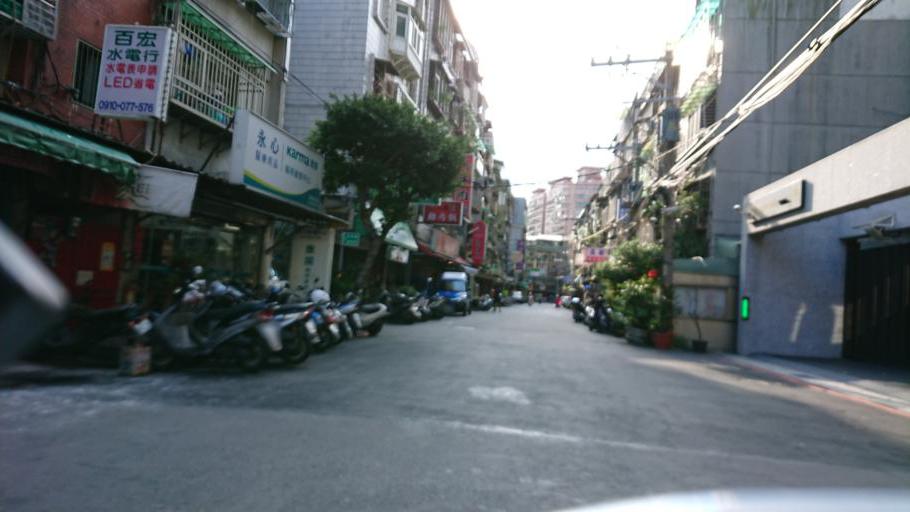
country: TW
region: Taipei
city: Taipei
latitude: 25.0855
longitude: 121.4803
